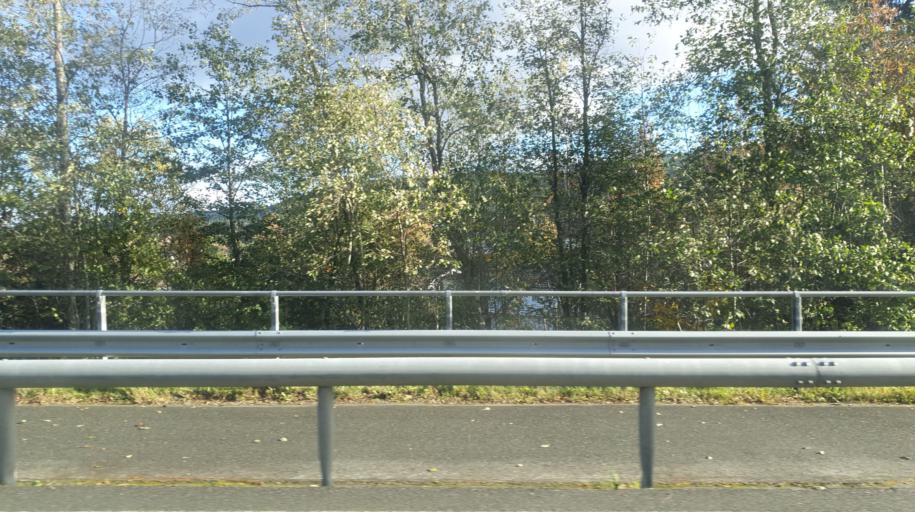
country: NO
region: Sor-Trondelag
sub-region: Klaebu
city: Klaebu
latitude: 63.3008
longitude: 10.4709
